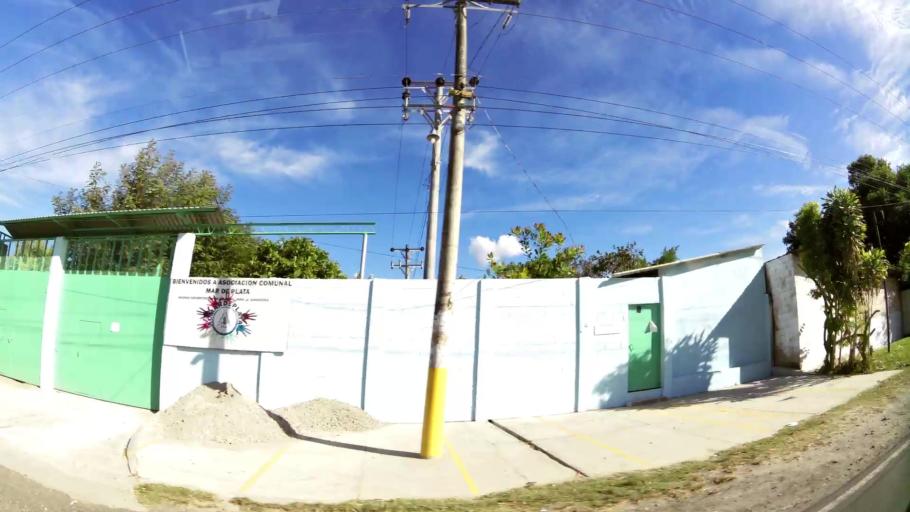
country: SV
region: Cuscatlan
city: Tecoluca
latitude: 13.7884
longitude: -89.0456
